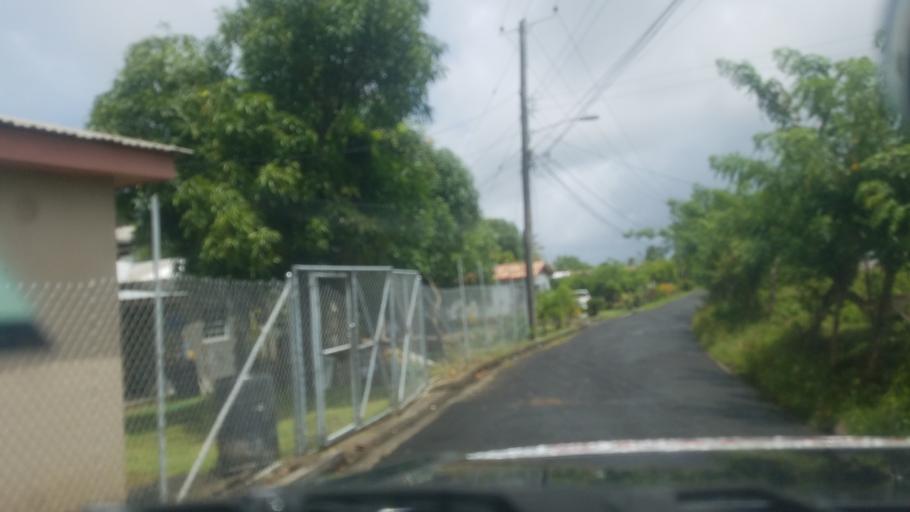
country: LC
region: Laborie Quarter
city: Laborie
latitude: 13.7590
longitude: -60.9761
